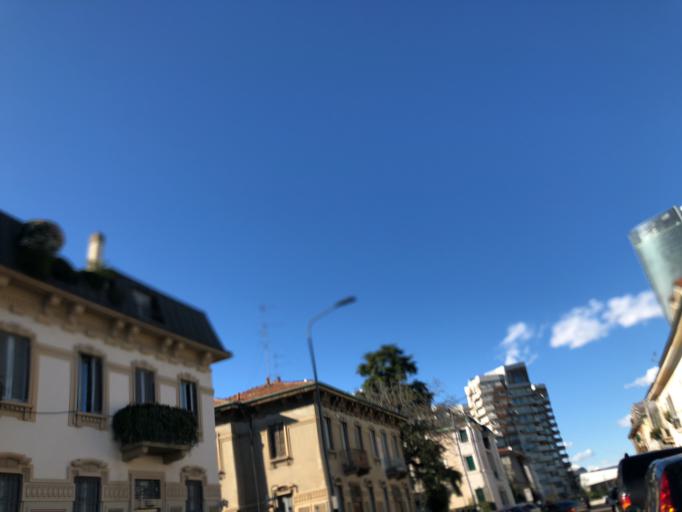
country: IT
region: Lombardy
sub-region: Citta metropolitana di Milano
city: Milano
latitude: 45.4741
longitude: 9.1538
